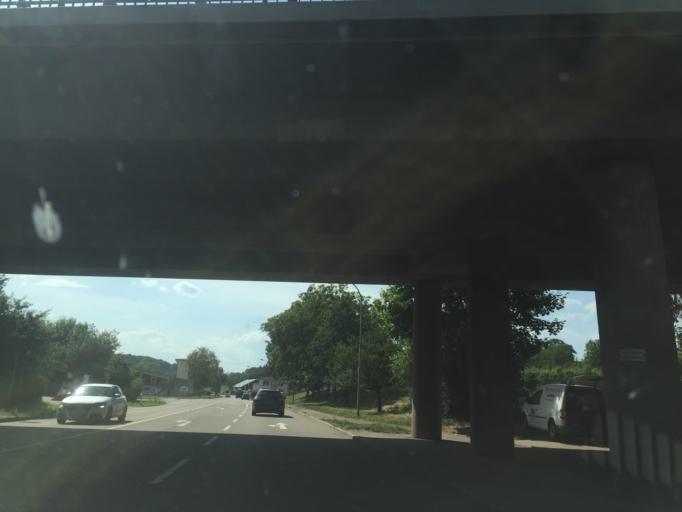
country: DE
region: Baden-Wuerttemberg
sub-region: Karlsruhe Region
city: Sinsheim
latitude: 49.2573
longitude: 8.8637
